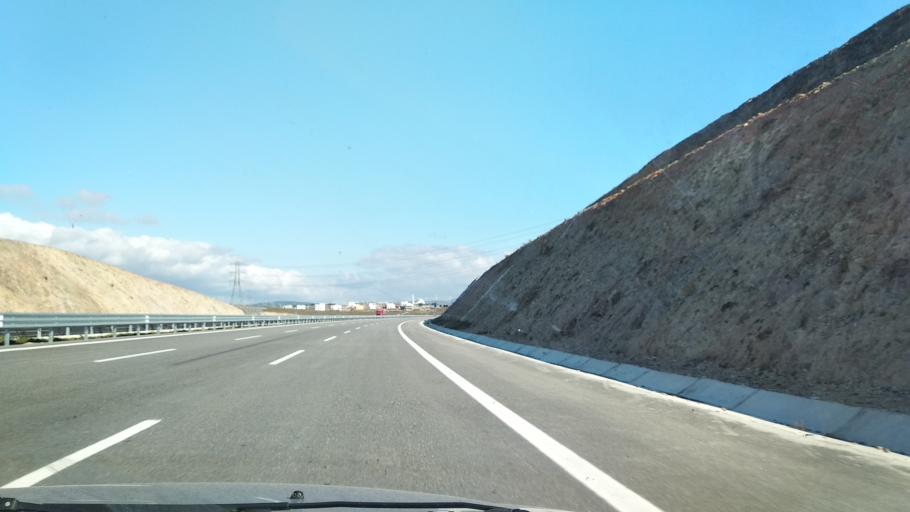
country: TR
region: Izmir
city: Yenisakran
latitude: 38.8509
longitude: 27.0530
